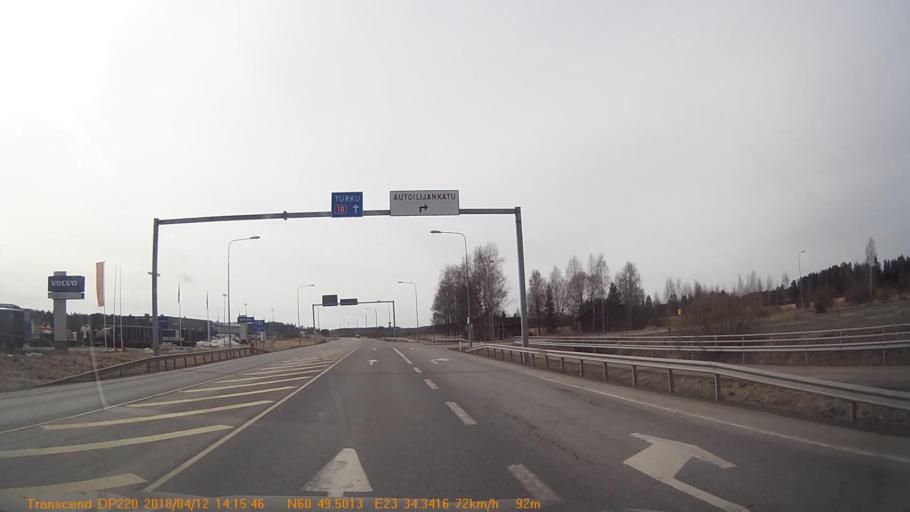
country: FI
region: Haeme
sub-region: Forssa
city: Forssa
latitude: 60.8250
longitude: 23.5719
